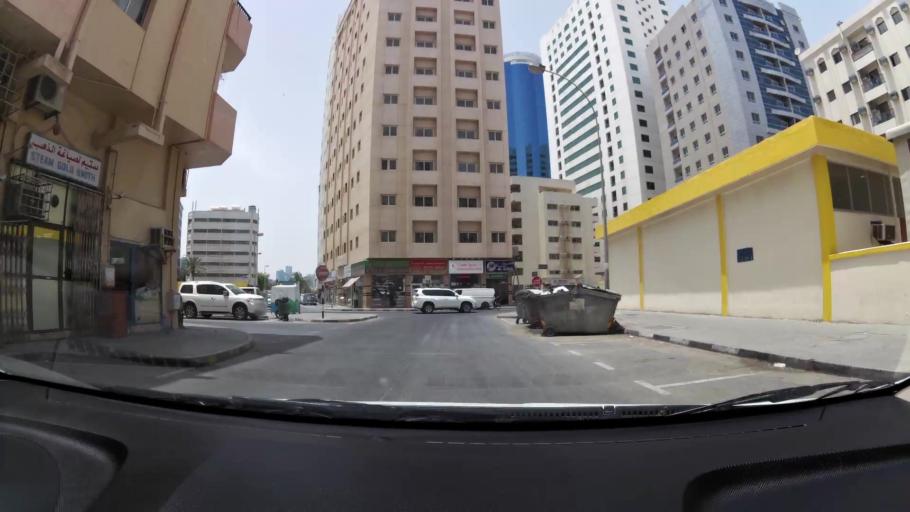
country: AE
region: Ash Shariqah
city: Sharjah
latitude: 25.3529
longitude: 55.3868
